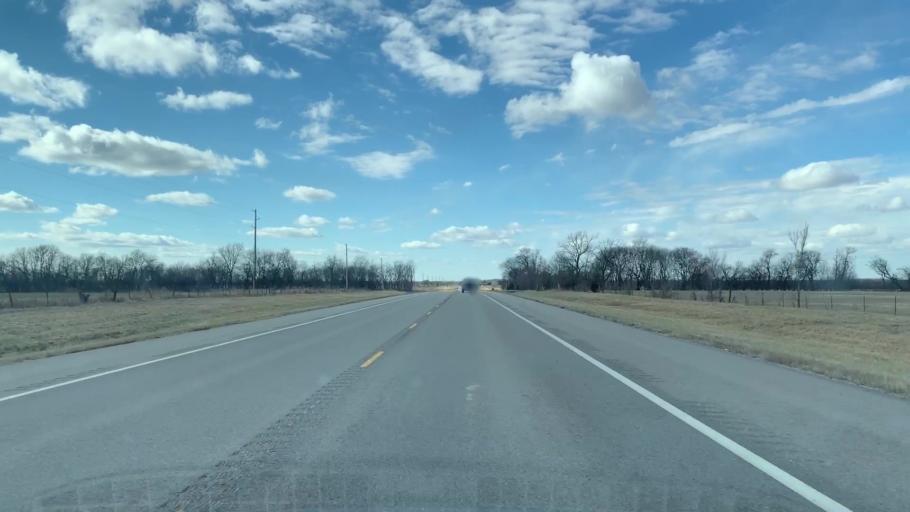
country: US
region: Kansas
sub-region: Labette County
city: Oswego
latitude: 37.3401
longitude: -95.0373
